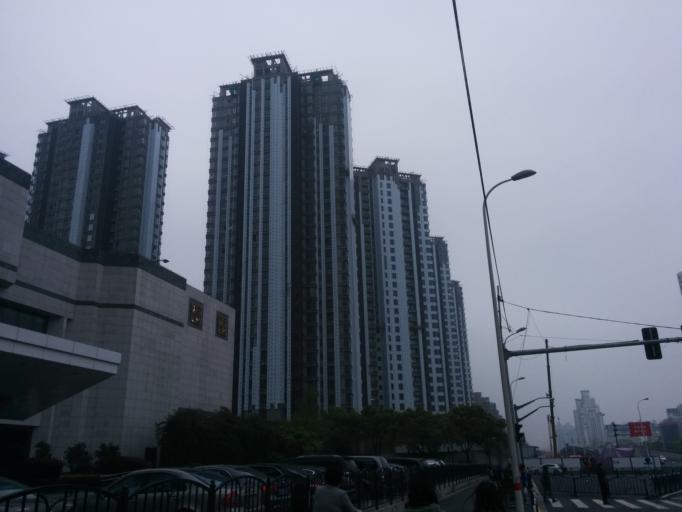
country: CN
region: Shanghai Shi
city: Huamu
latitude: 31.2135
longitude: 121.5293
